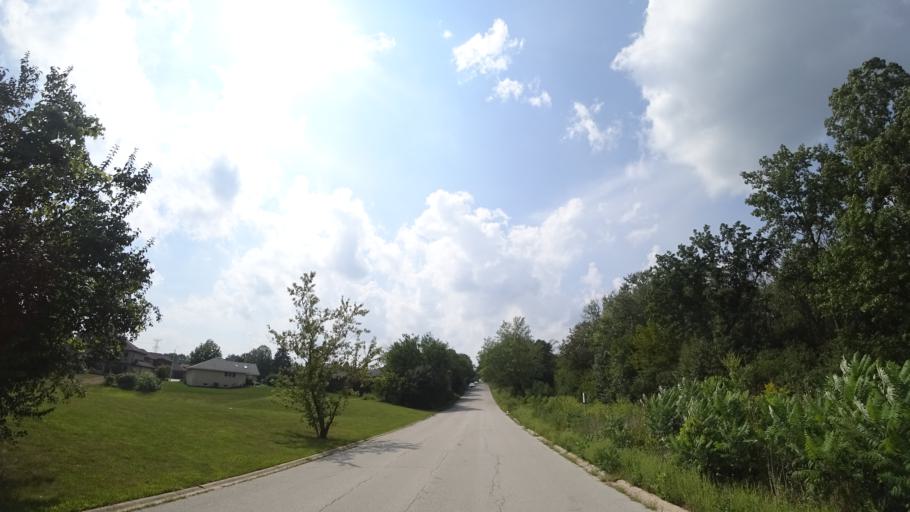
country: US
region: Illinois
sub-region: Will County
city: Goodings Grove
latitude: 41.6442
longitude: -87.9041
